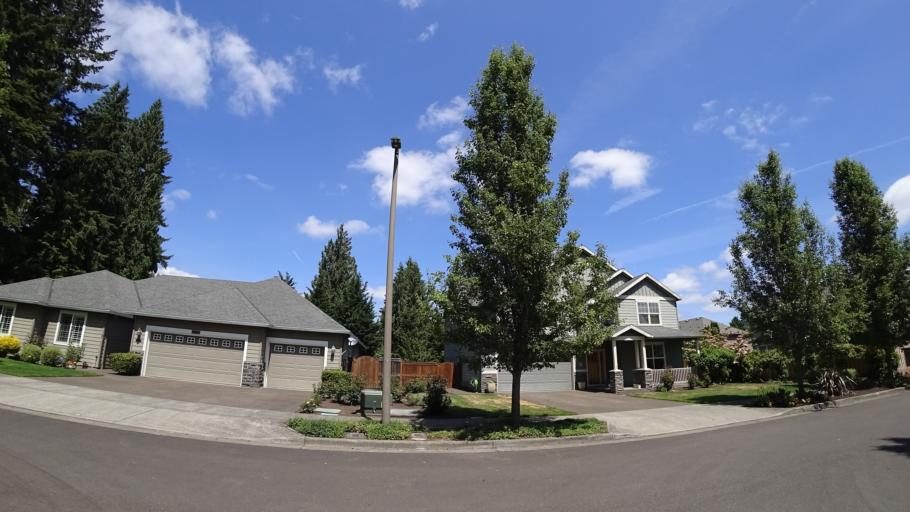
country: US
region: Oregon
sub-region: Washington County
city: Tigard
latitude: 45.4291
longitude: -122.7972
